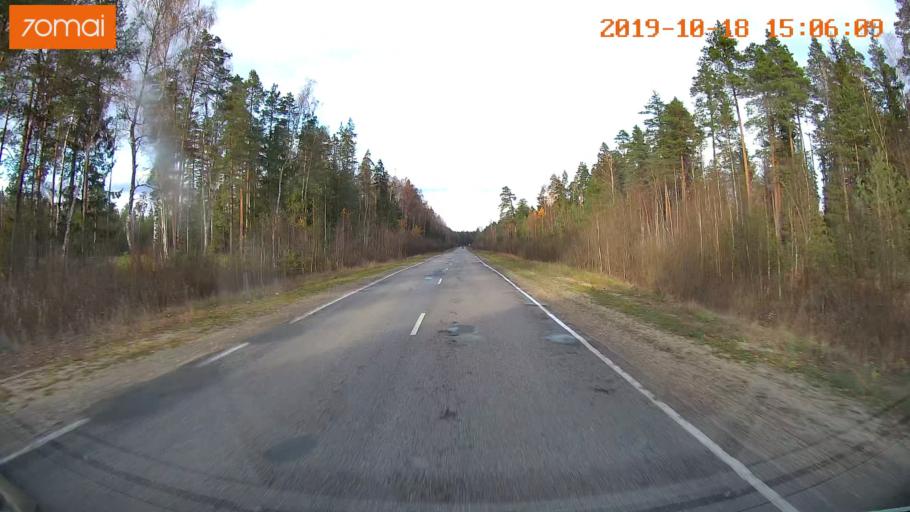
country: RU
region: Vladimir
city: Gus'-Khrustal'nyy
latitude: 55.5256
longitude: 40.5765
